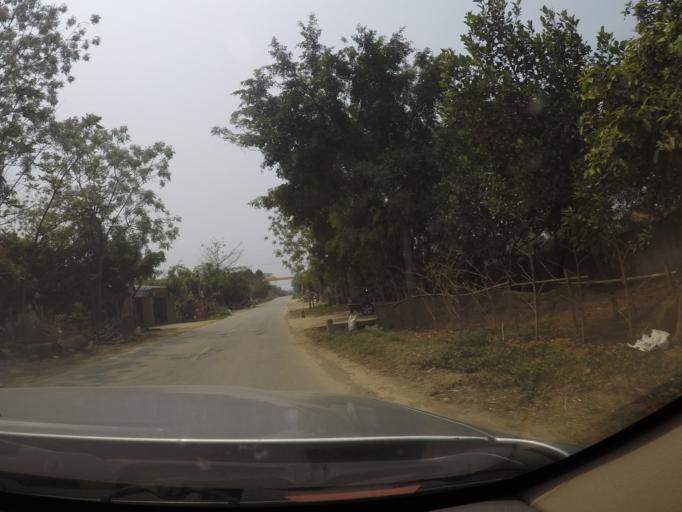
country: VN
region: Thanh Hoa
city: Thi Tran Thuong Xuan
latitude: 19.8345
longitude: 105.3964
